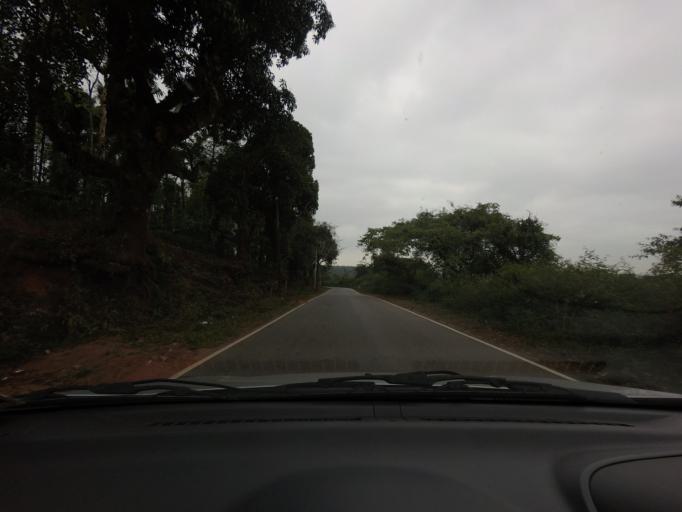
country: IN
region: Karnataka
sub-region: Hassan
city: Sakleshpur
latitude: 12.9363
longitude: 75.7623
